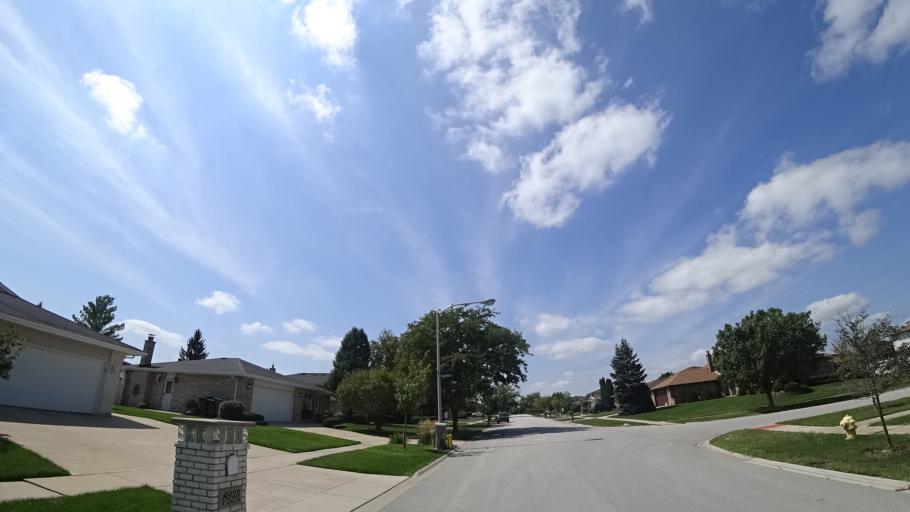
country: US
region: Illinois
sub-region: Cook County
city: Orland Hills
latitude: 41.5676
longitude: -87.8360
